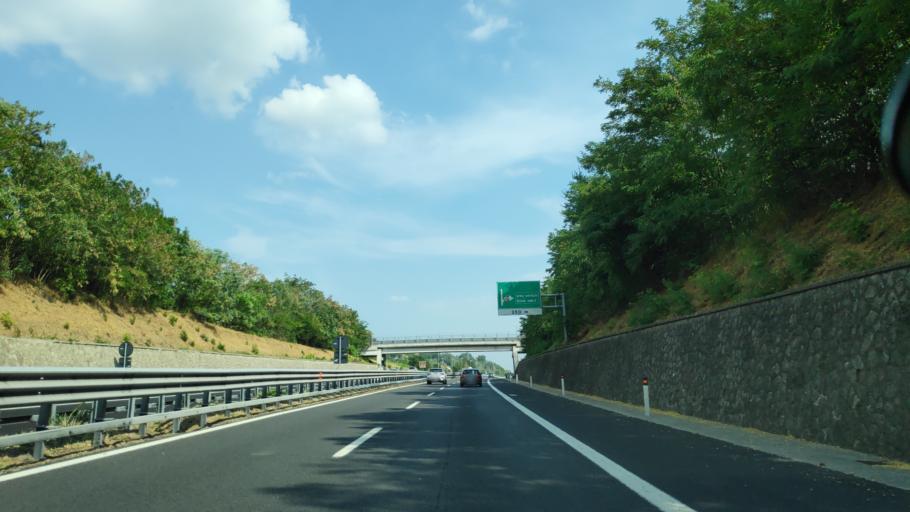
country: IT
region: Umbria
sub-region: Provincia di Terni
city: Attigliano
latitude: 42.5026
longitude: 12.3071
